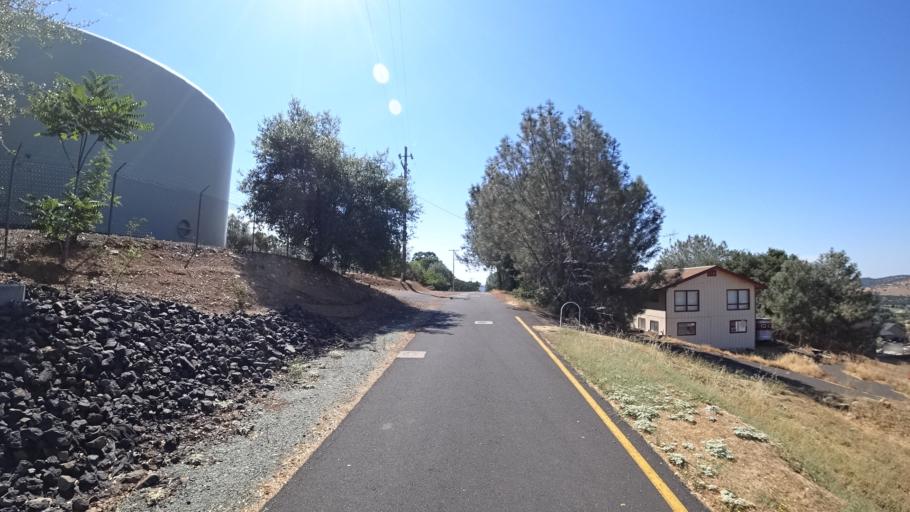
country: US
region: California
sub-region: Calaveras County
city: Copperopolis
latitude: 37.9294
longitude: -120.6331
